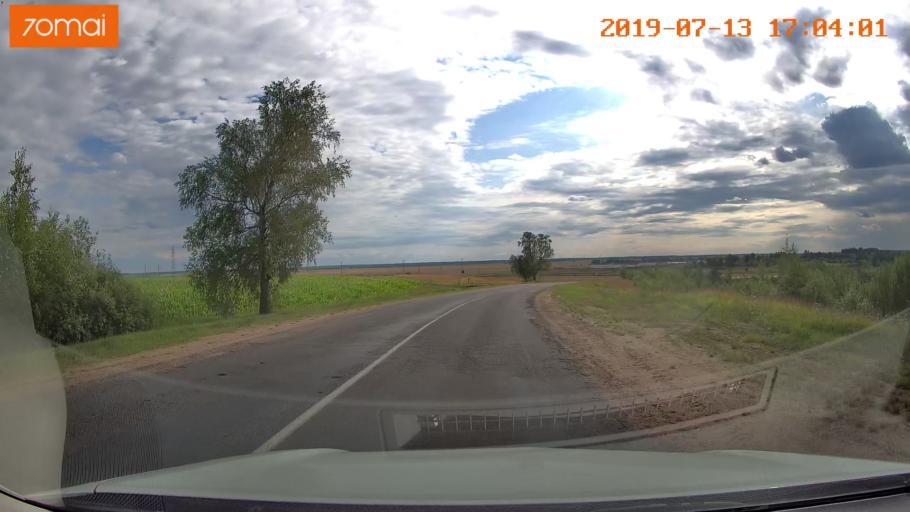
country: BY
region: Mogilev
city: Kirawsk
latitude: 53.2719
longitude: 29.3731
